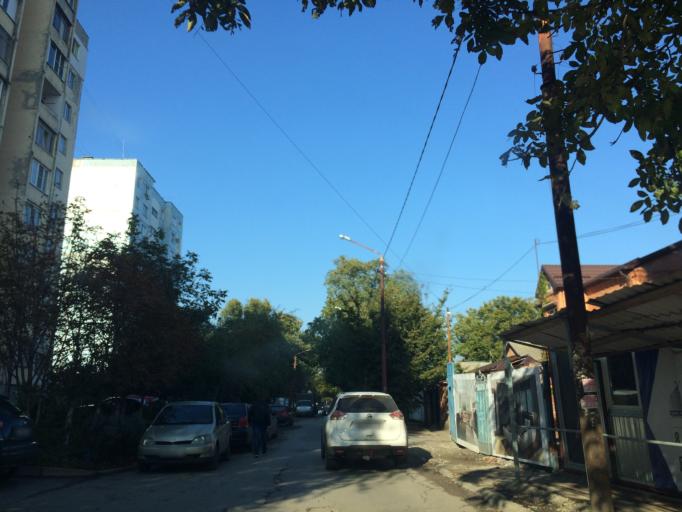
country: RU
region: Rostov
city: Rostov-na-Donu
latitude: 47.2200
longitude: 39.6625
